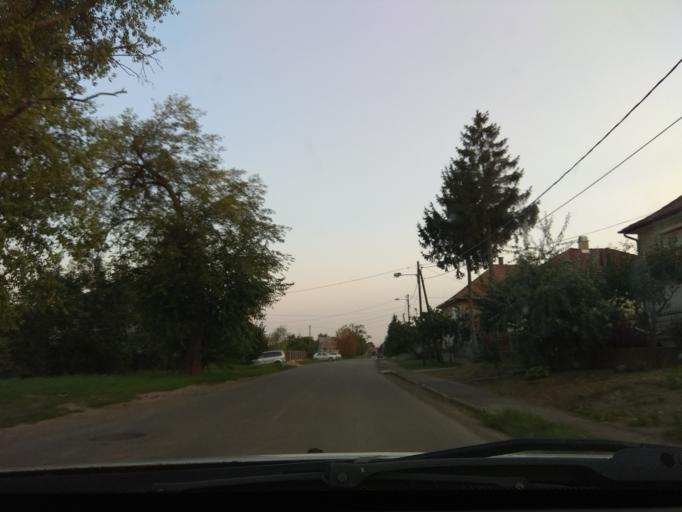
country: HU
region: Borsod-Abauj-Zemplen
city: Szerencs
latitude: 48.1965
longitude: 21.2147
